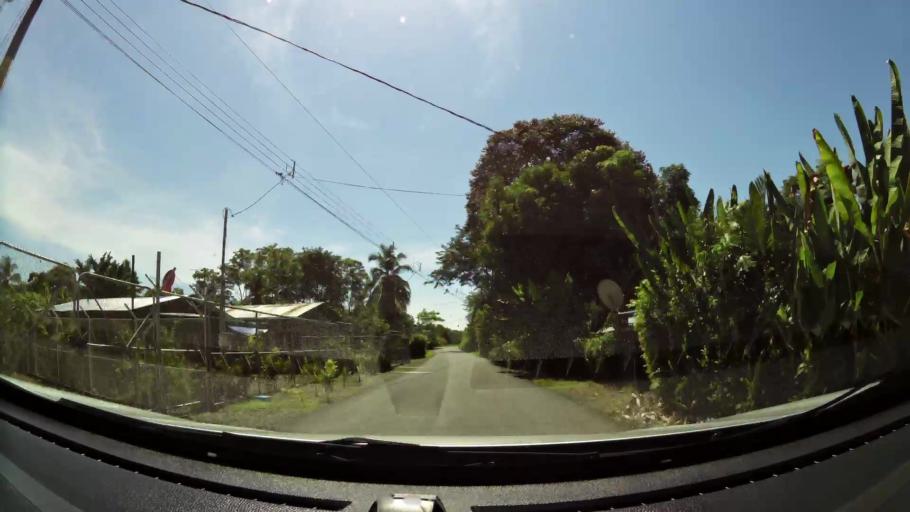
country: CR
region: Puntarenas
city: Quepos
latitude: 9.3293
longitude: -83.9572
